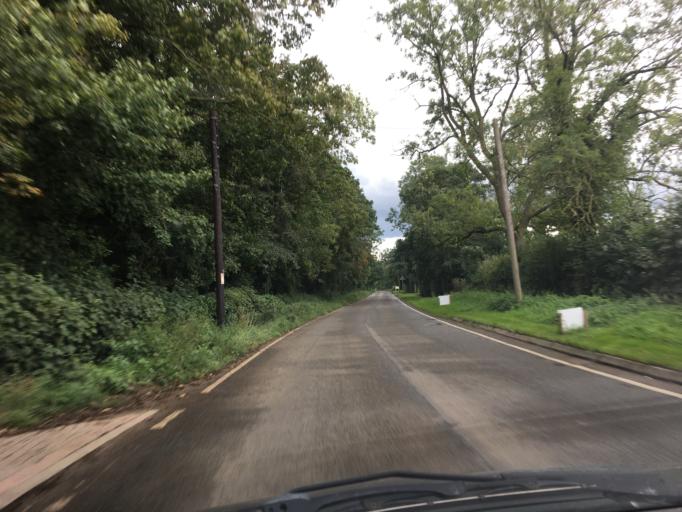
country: GB
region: England
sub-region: Leicestershire
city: Lutterworth
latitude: 52.4787
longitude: -1.2120
